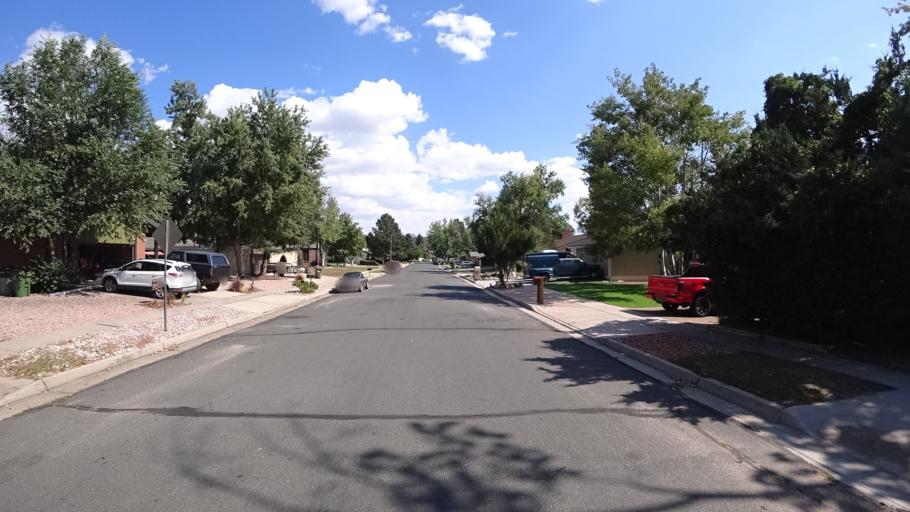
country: US
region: Colorado
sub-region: El Paso County
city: Cimarron Hills
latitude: 38.8736
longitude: -104.7537
